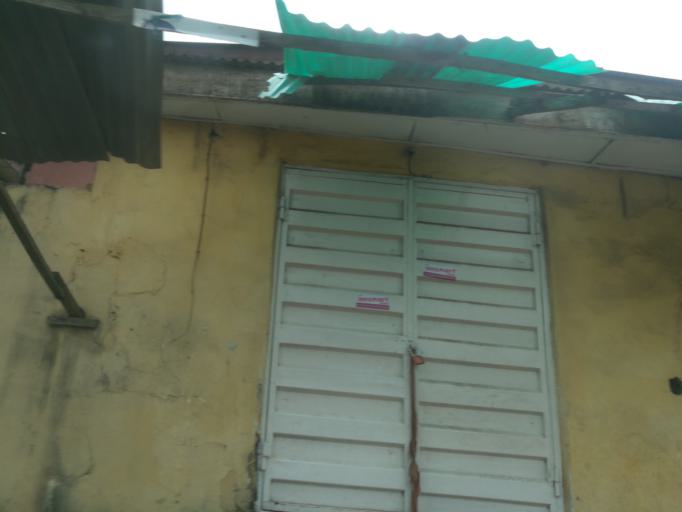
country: NG
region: Lagos
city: Oshodi
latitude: 6.5805
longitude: 3.3053
